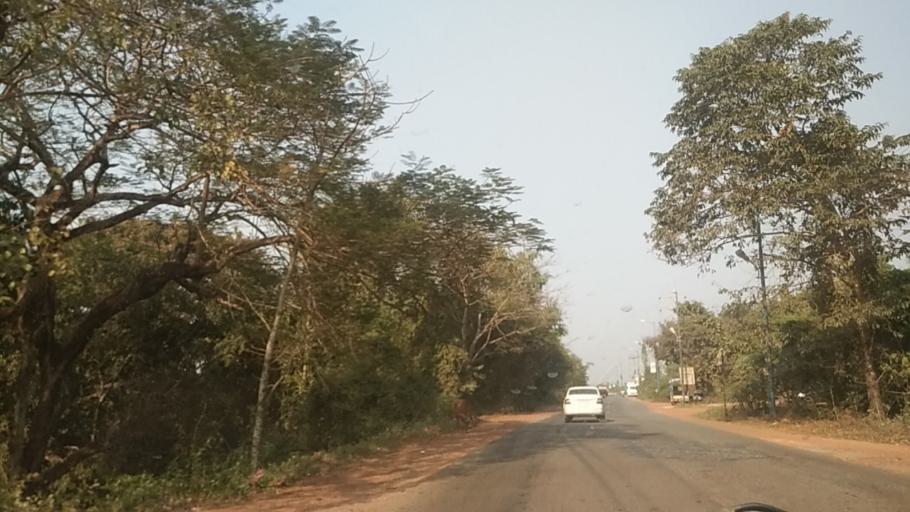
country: IN
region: Goa
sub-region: North Goa
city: Colovale
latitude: 15.6461
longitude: 73.8350
